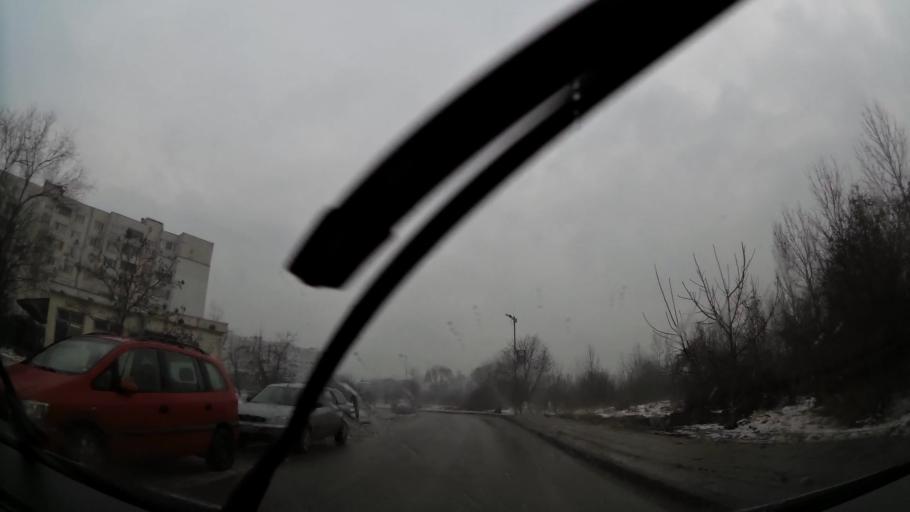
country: BG
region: Sofia-Capital
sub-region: Stolichna Obshtina
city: Sofia
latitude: 42.6862
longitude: 23.2641
